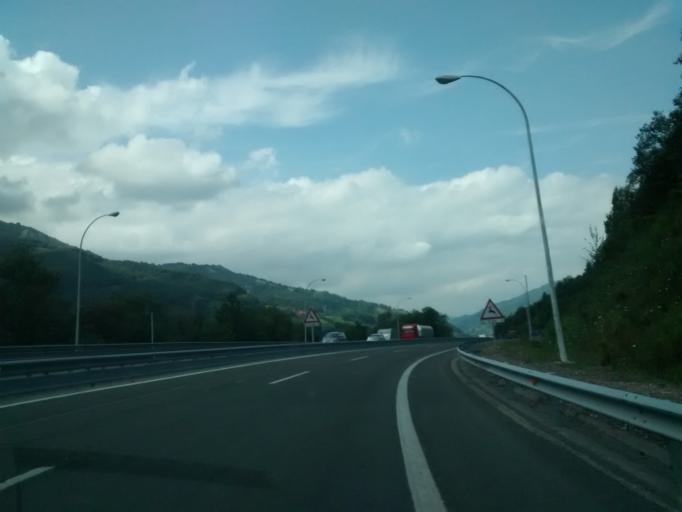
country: ES
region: Asturias
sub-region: Province of Asturias
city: Pola de Lena
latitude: 43.0903
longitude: -5.8234
